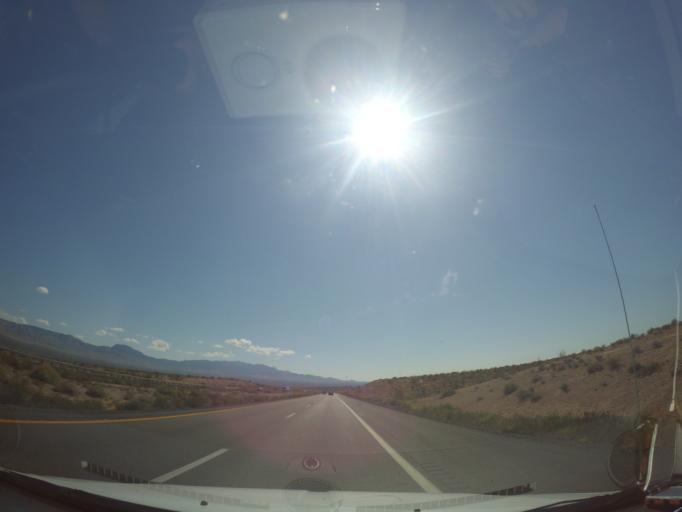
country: US
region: Nevada
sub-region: Clark County
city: Mesquite
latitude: 36.8385
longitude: -114.0000
